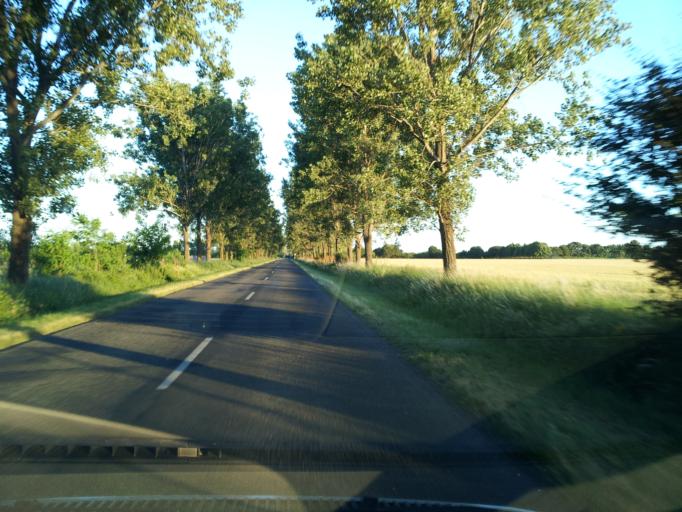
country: HU
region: Veszprem
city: Szentkiralyszabadja
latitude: 47.0525
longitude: 17.9285
